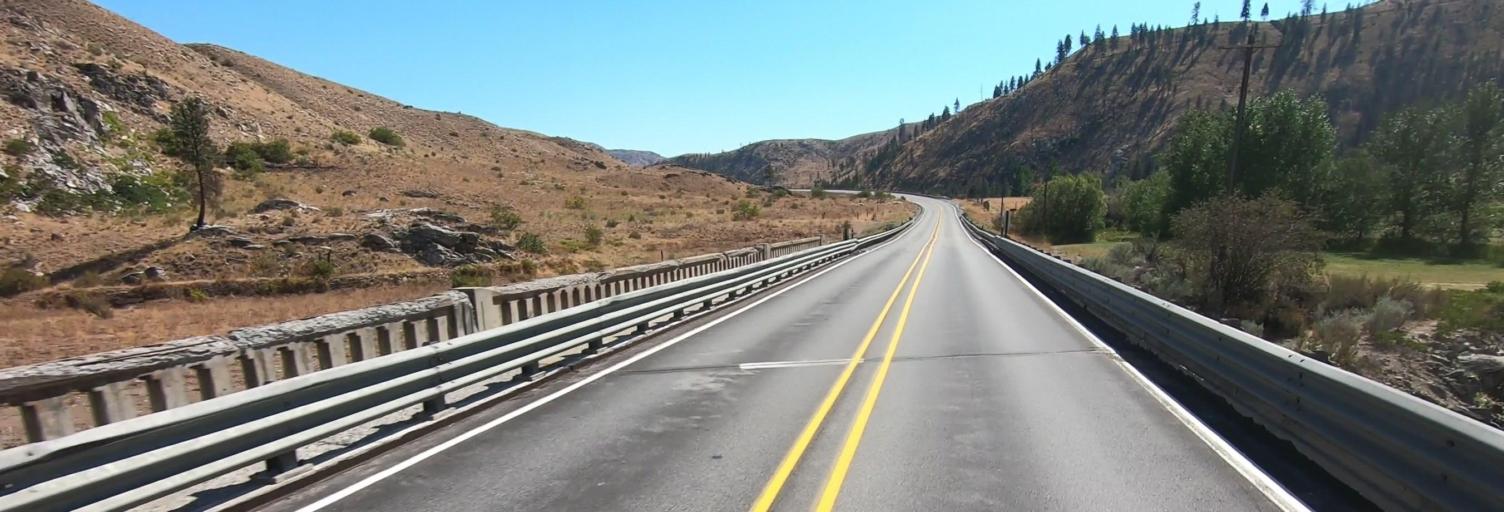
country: US
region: Washington
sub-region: Okanogan County
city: Brewster
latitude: 48.1464
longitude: -120.0468
